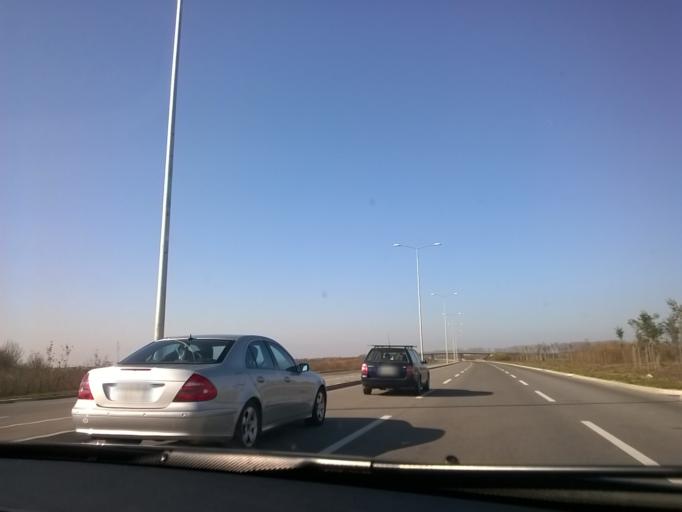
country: RS
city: Ovca
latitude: 44.9129
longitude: 20.5046
